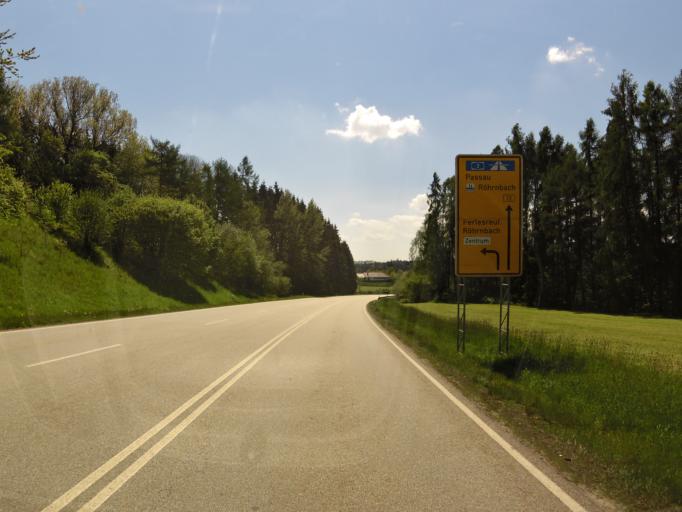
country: DE
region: Bavaria
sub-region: Lower Bavaria
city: Roehrnbach
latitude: 48.7485
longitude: 13.5164
